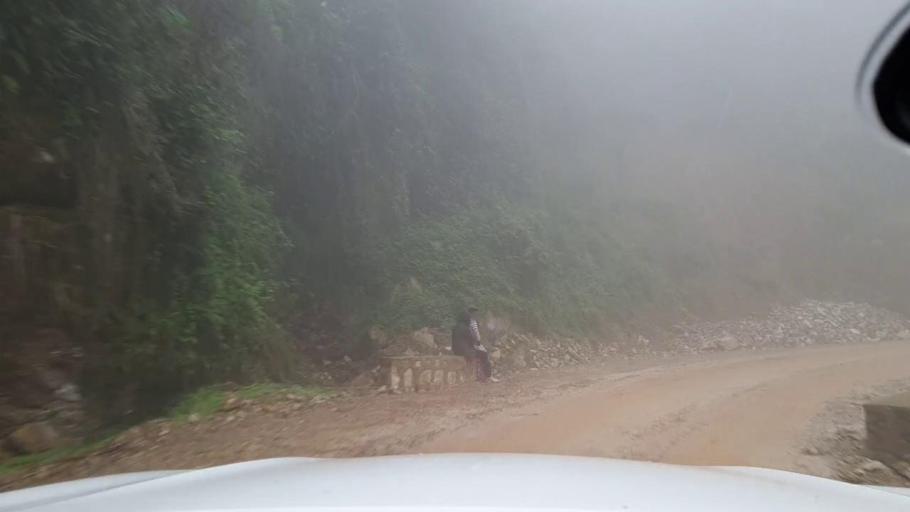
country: BI
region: Cibitoke
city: Cibitoke
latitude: -2.5951
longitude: 29.1951
